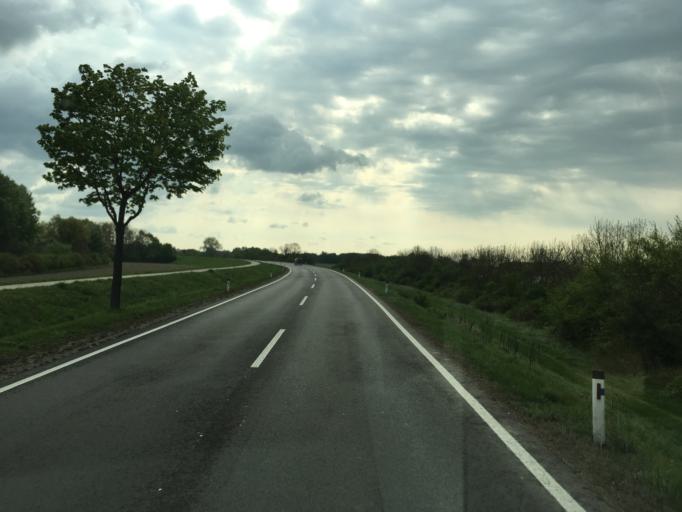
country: AT
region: Lower Austria
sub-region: Politischer Bezirk Bruck an der Leitha
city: Berg
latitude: 48.1222
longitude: 17.0445
